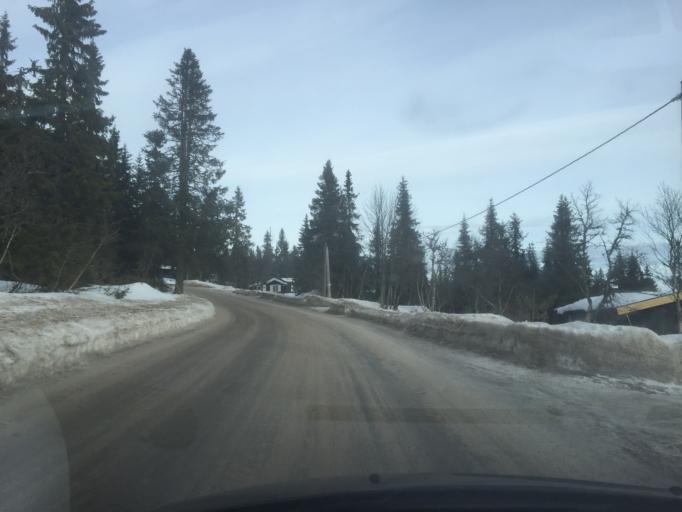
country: NO
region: Hedmark
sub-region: Trysil
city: Innbygda
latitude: 61.3256
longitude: 12.1523
